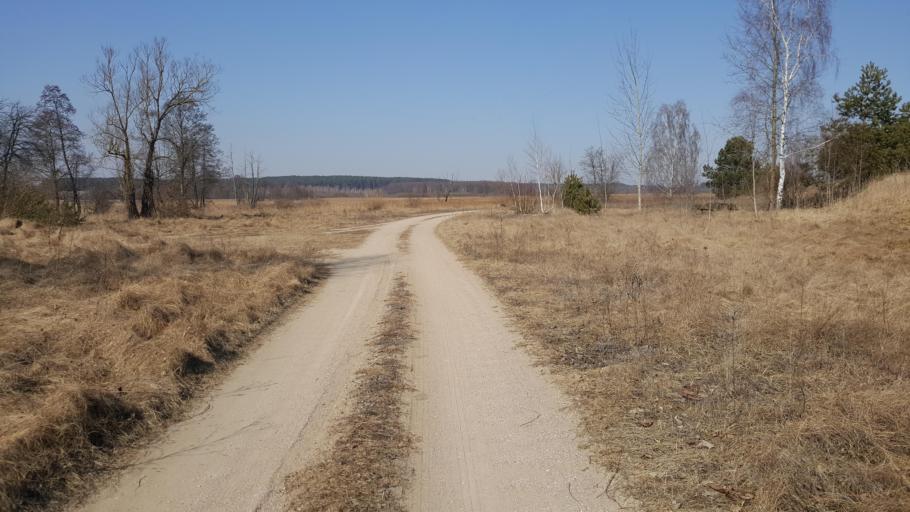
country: BY
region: Brest
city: Kamyanyets
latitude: 52.3654
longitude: 23.7446
